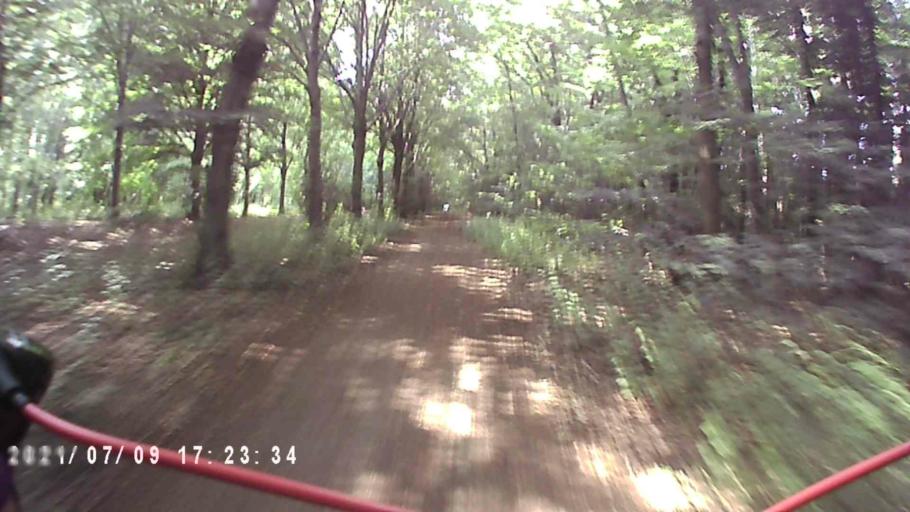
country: NL
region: Groningen
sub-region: Gemeente Vlagtwedde
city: Vlagtwedde
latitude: 53.0859
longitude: 7.1540
